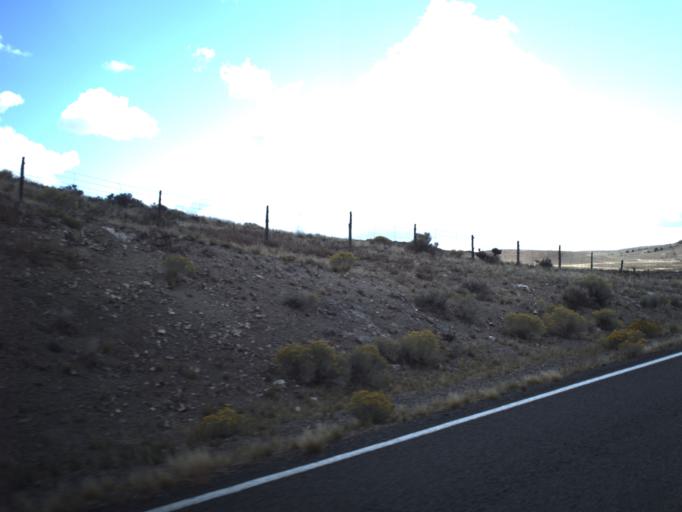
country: US
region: Utah
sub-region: Beaver County
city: Milford
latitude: 38.6279
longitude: -113.8518
